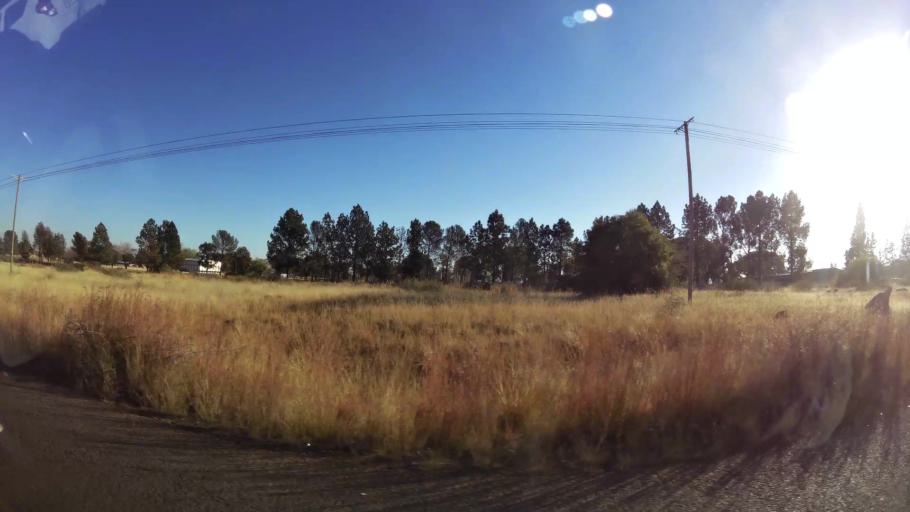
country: ZA
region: Northern Cape
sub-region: Frances Baard District Municipality
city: Kimberley
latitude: -28.7431
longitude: 24.7192
